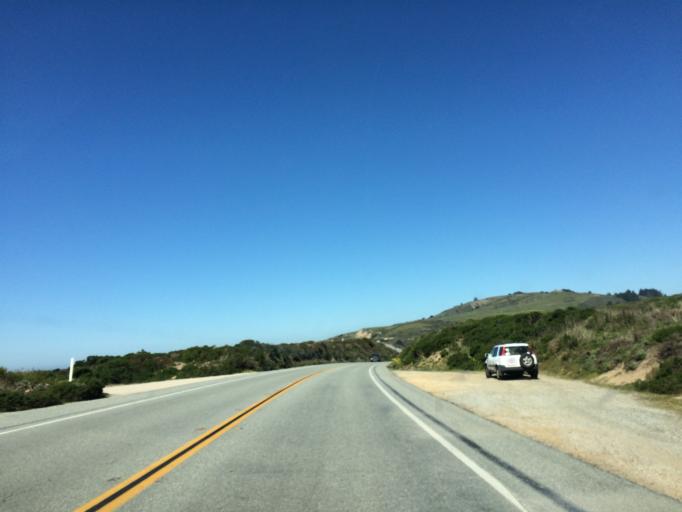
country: US
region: California
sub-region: Santa Cruz County
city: Bonny Doon
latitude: 37.0342
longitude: -122.2249
